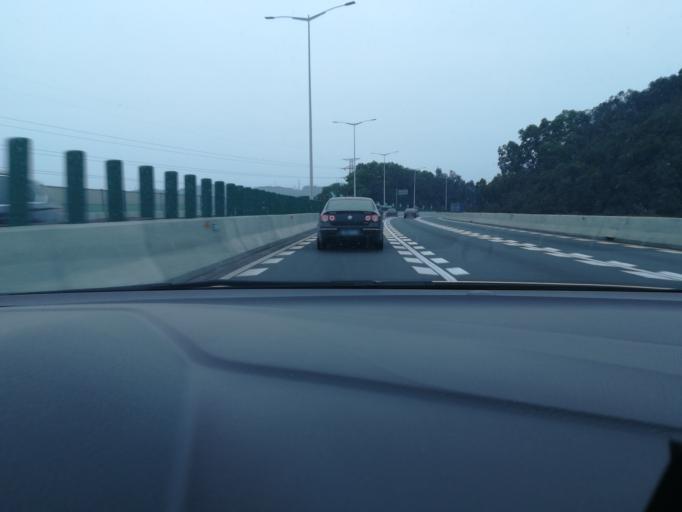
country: CN
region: Guangdong
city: Longdong
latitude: 23.2381
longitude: 113.3513
